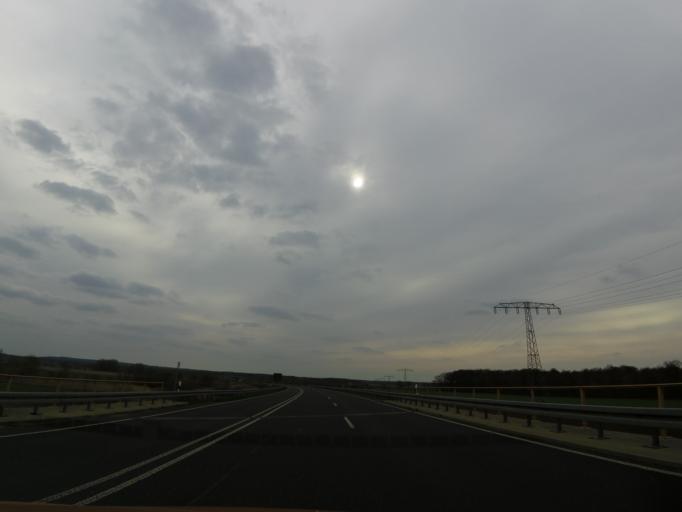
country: DE
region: Brandenburg
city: Mullrose
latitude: 52.2579
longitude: 14.4017
